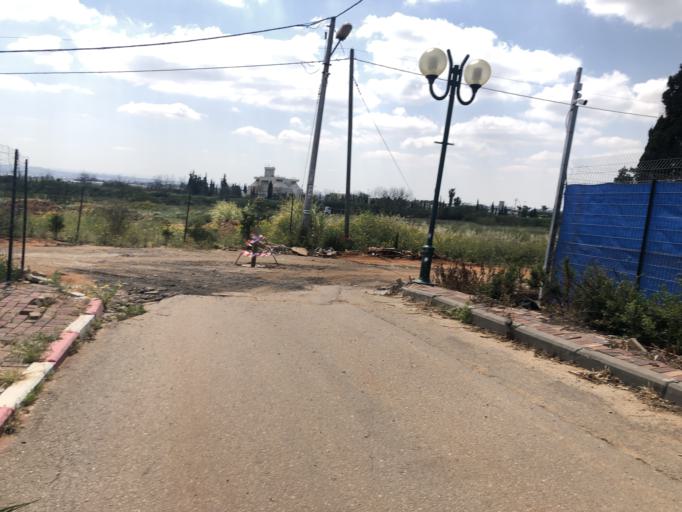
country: IL
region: Central District
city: Hod HaSharon
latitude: 32.1530
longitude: 34.9140
